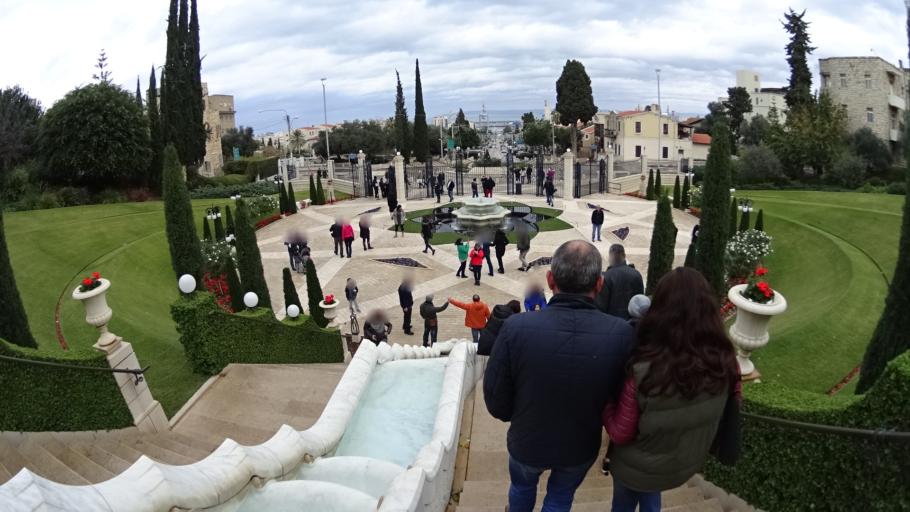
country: IL
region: Haifa
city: Haifa
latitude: 32.8170
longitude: 34.9886
